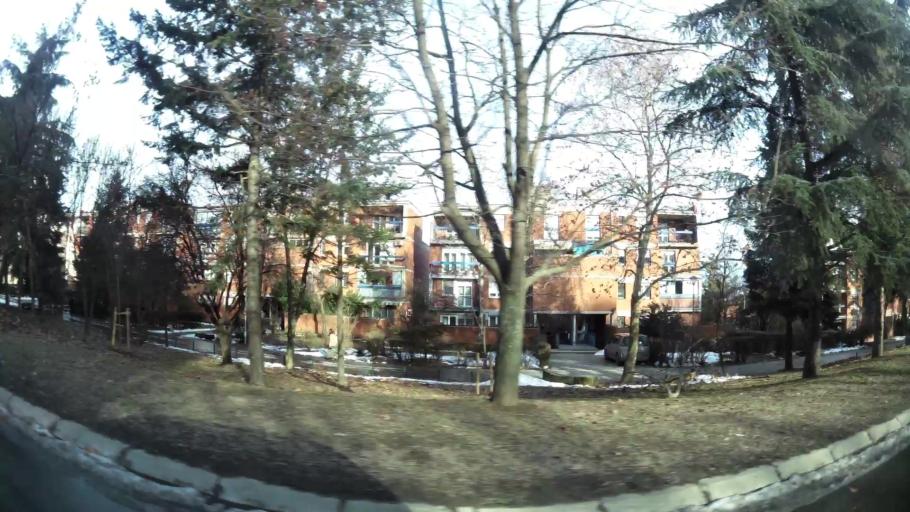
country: RS
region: Central Serbia
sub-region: Belgrade
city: Rakovica
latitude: 44.7292
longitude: 20.4250
